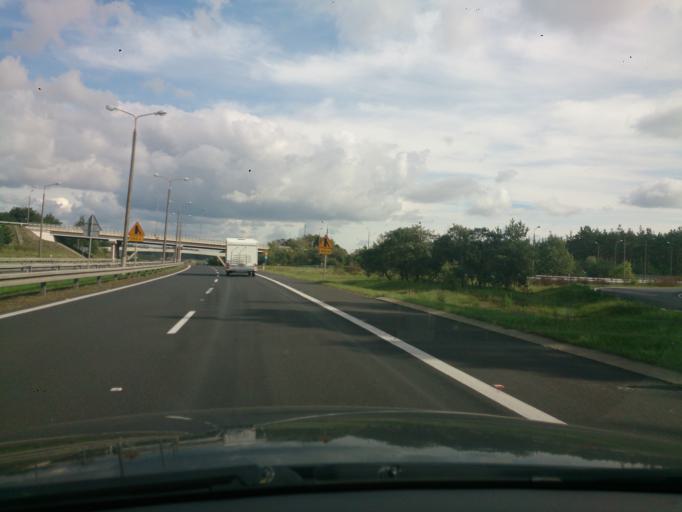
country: PL
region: Kujawsko-Pomorskie
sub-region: Powiat swiecki
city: Swiecie
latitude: 53.4069
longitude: 18.3808
